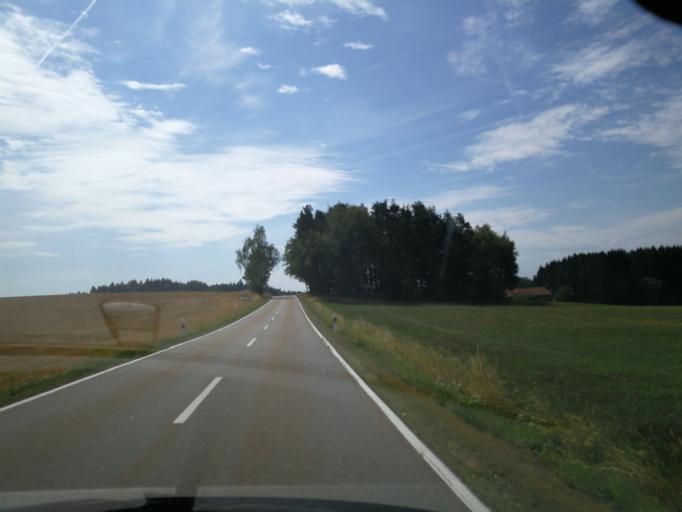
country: DE
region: Bavaria
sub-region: Lower Bavaria
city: Falkenfels
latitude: 49.0538
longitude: 12.5853
